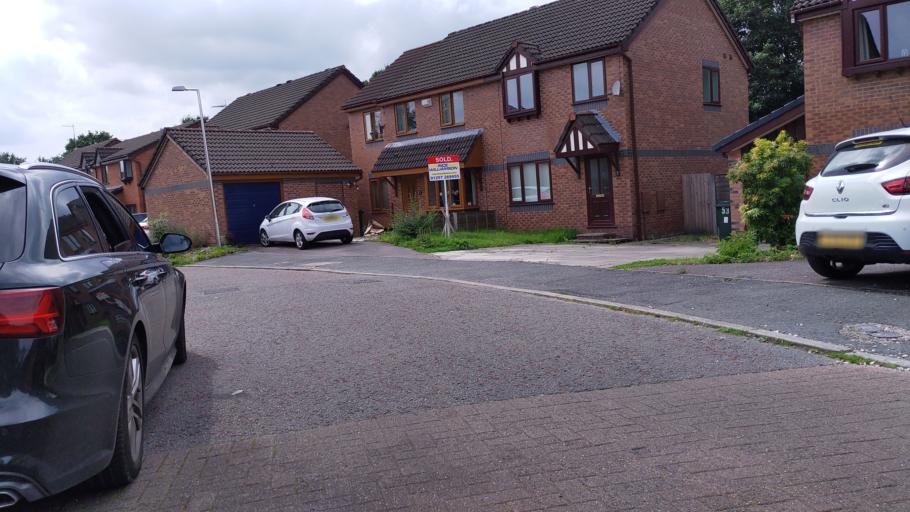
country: GB
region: England
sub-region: Lancashire
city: Coppull
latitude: 53.6328
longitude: -2.6349
